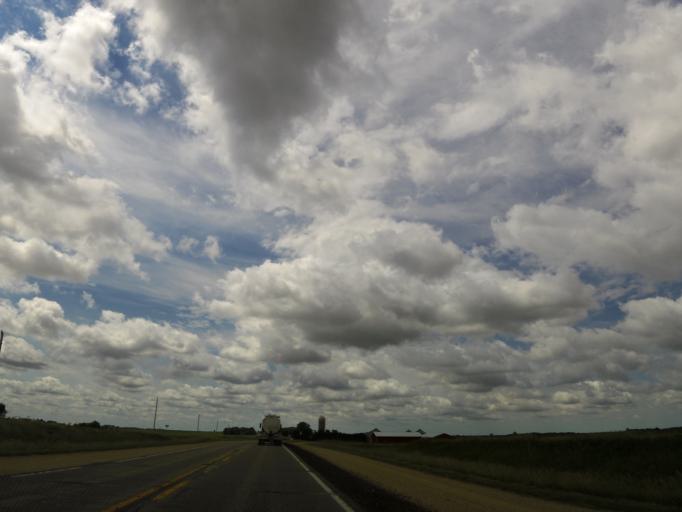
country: US
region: Iowa
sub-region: Howard County
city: Cresco
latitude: 43.3215
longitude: -92.2989
